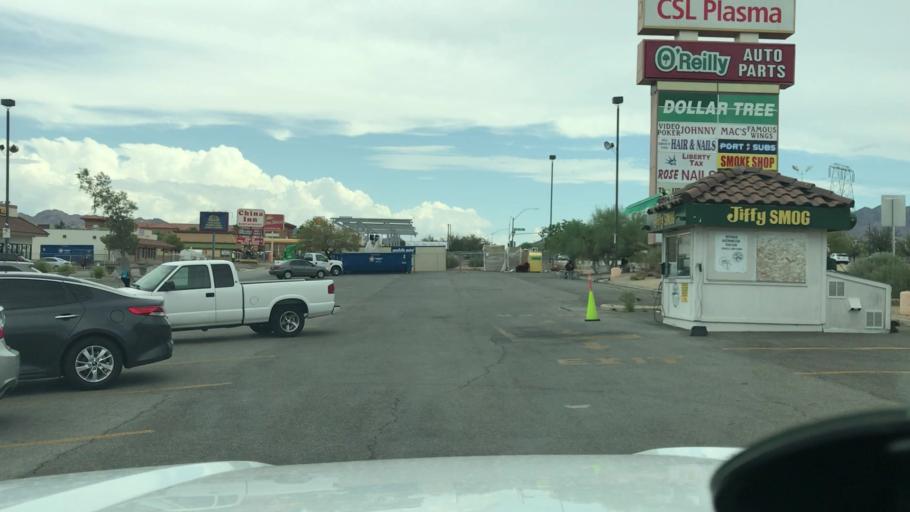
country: US
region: Nevada
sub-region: Clark County
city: Henderson
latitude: 36.0260
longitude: -114.9660
